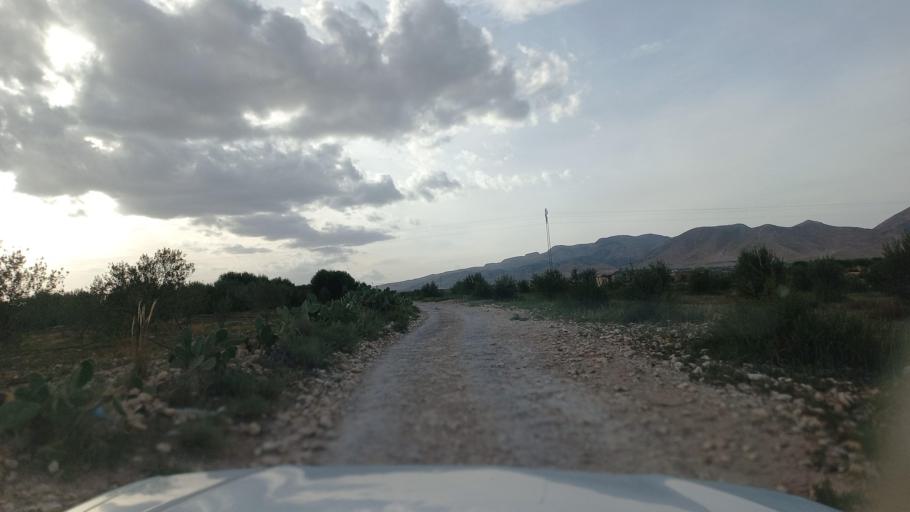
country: TN
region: Al Qasrayn
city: Sbiba
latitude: 35.4362
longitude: 9.0970
